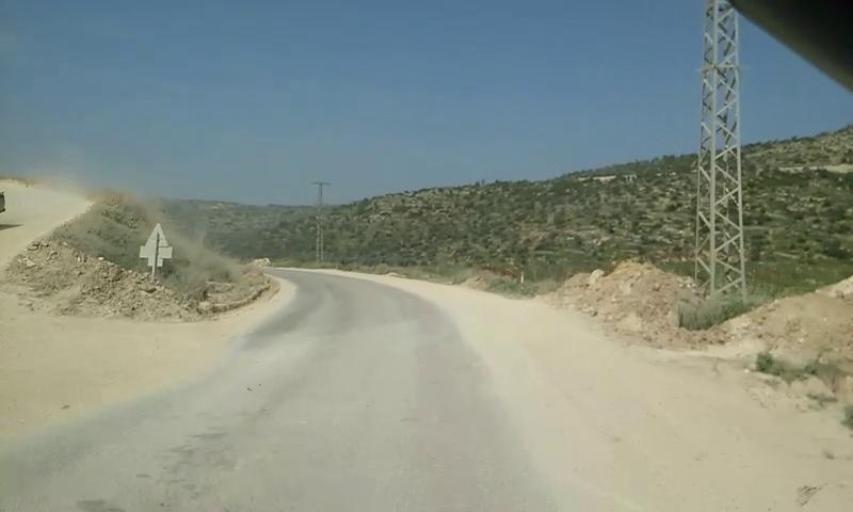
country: PS
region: West Bank
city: Az Zababidah
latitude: 32.4038
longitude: 35.3164
